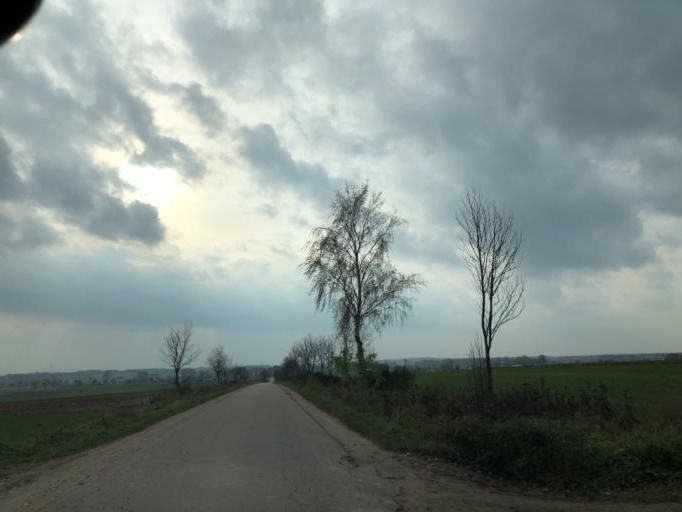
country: PL
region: Podlasie
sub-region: Powiat lomzynski
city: Sniadowo
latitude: 53.1262
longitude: 21.9651
